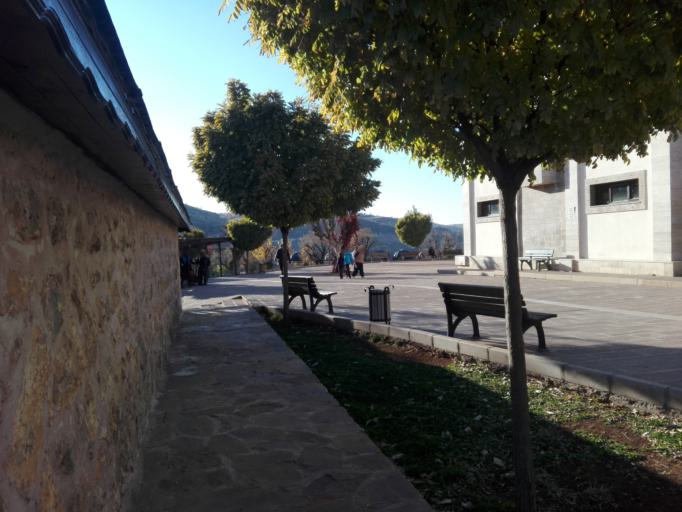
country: TR
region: Diyarbakir
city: Egil
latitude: 38.2536
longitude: 40.0991
